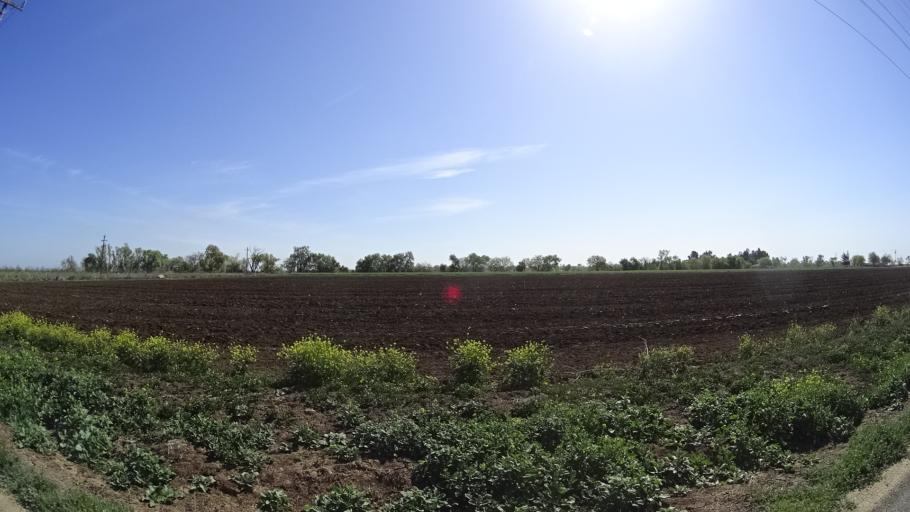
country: US
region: California
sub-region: Glenn County
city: Willows
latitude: 39.5422
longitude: -122.1866
